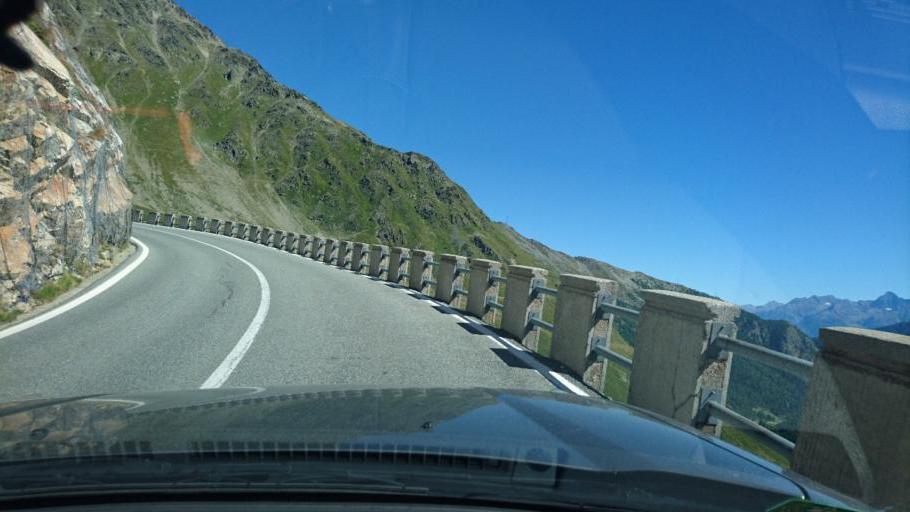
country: IT
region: Aosta Valley
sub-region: Valle d'Aosta
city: San Leonardo
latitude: 45.8584
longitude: 7.1526
